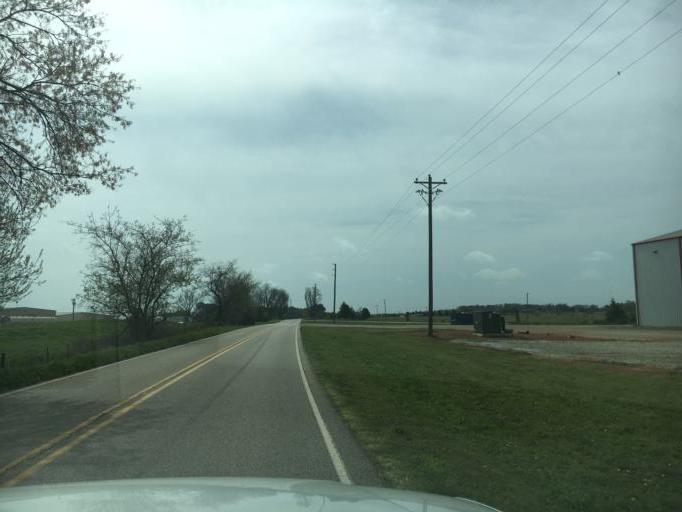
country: US
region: Georgia
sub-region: Hart County
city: Royston
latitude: 34.3045
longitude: -83.0456
